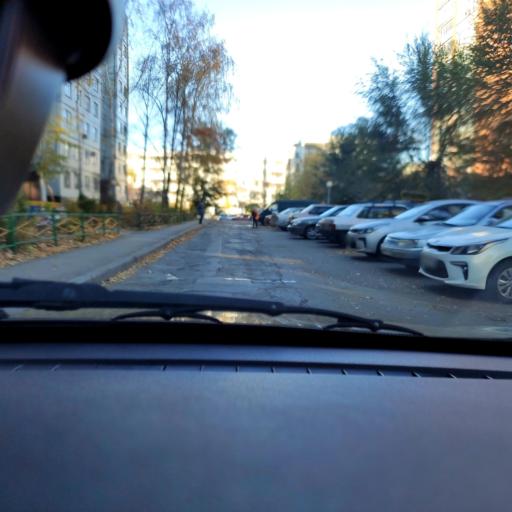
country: RU
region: Samara
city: Tol'yatti
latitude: 53.5227
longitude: 49.2885
